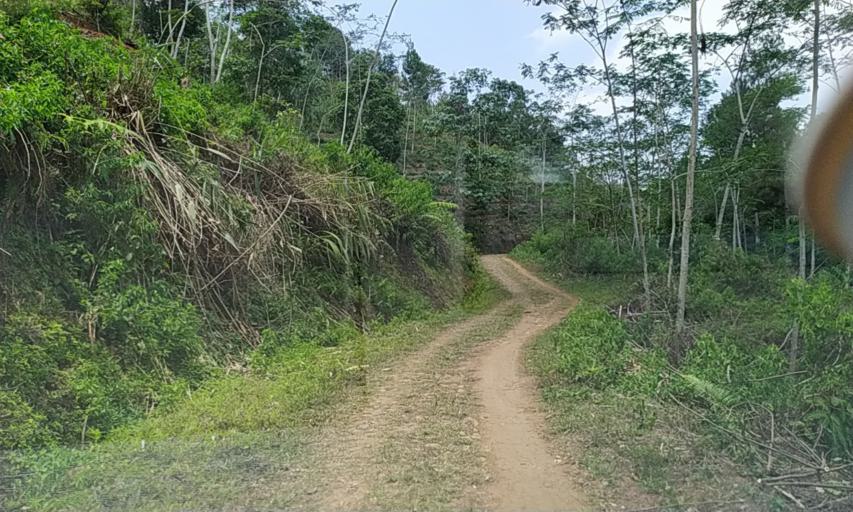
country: ID
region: Central Java
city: Timbang Satu
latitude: -7.1980
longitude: 108.6625
